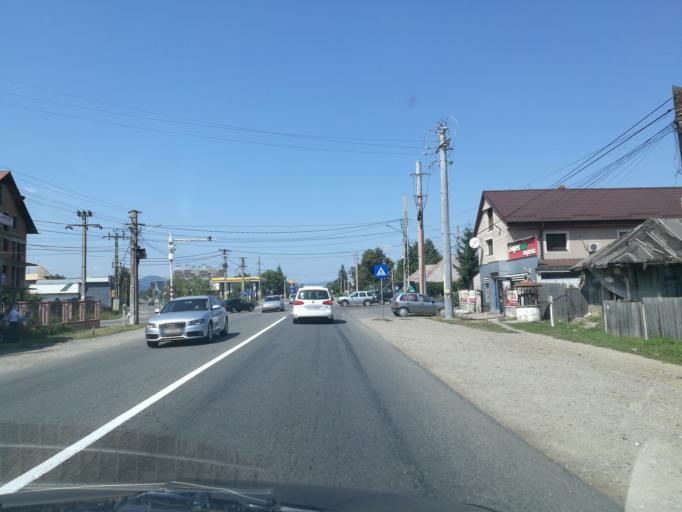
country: RO
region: Neamt
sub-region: Comuna Roznov
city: Chintinici
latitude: 46.8427
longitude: 26.4995
